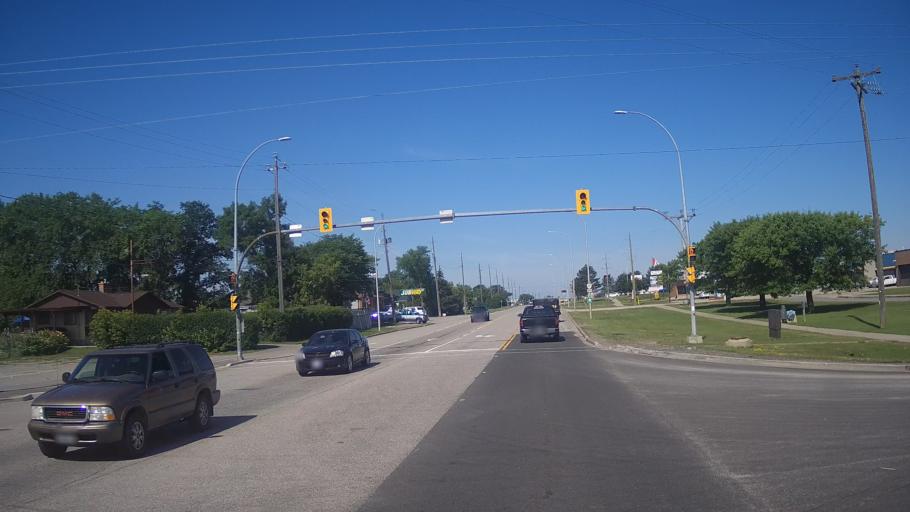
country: CA
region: Ontario
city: Dryden
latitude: 49.7862
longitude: -92.8240
